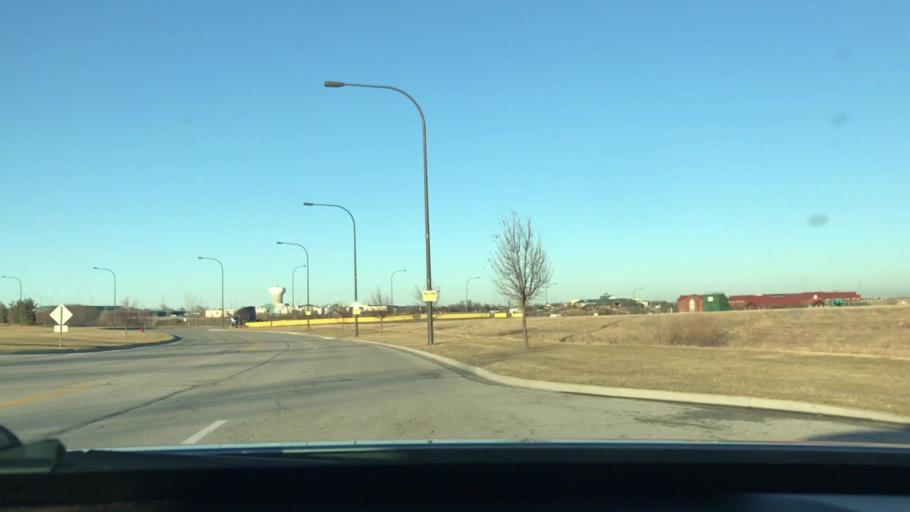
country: US
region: Kansas
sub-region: Wyandotte County
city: Edwardsville
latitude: 39.1117
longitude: -94.8243
